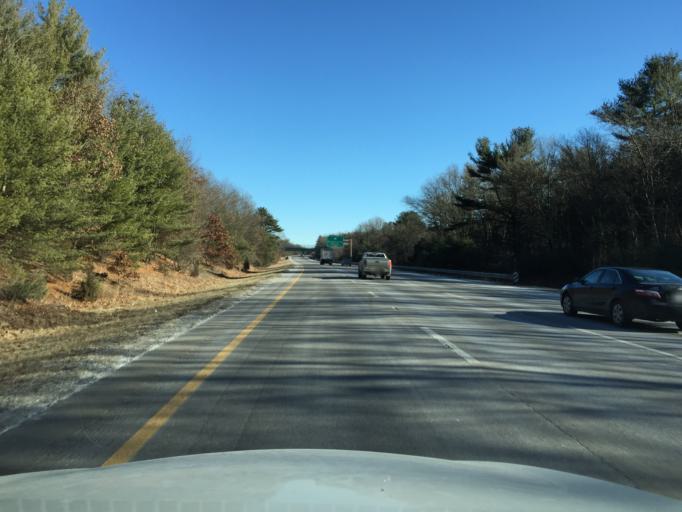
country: US
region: Massachusetts
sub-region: Norfolk County
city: Foxborough
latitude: 42.0318
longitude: -71.2791
